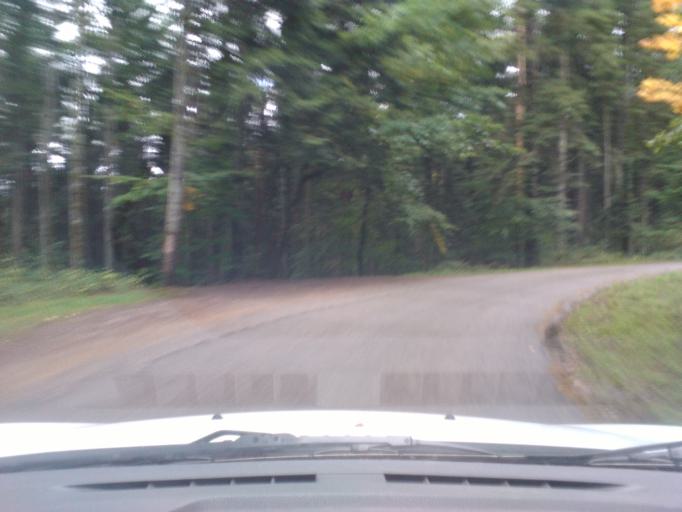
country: FR
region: Lorraine
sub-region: Departement des Vosges
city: Sainte-Marguerite
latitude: 48.2966
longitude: 6.9843
